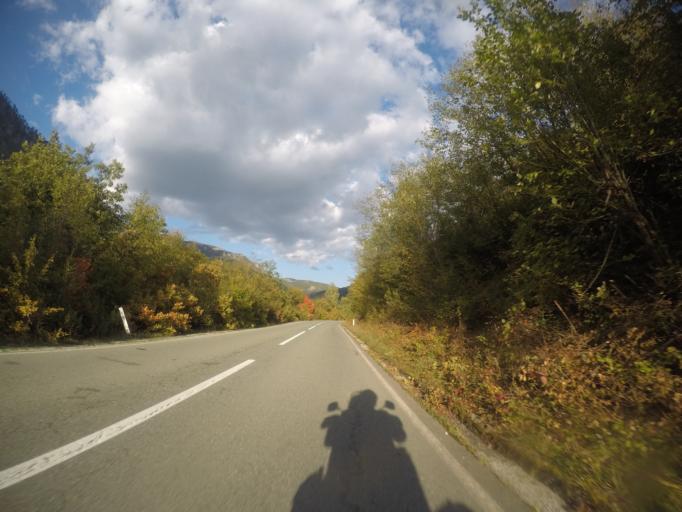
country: ME
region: Mojkovac
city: Mojkovac
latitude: 42.9910
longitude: 19.4238
